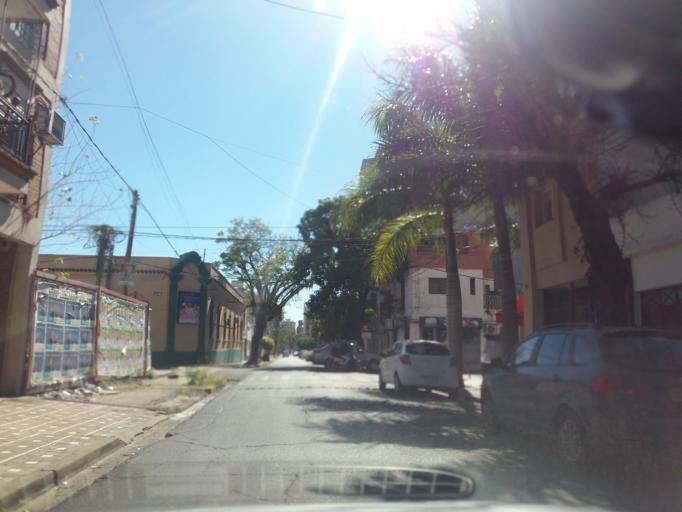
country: AR
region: Corrientes
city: Corrientes
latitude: -27.4706
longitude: -58.8432
